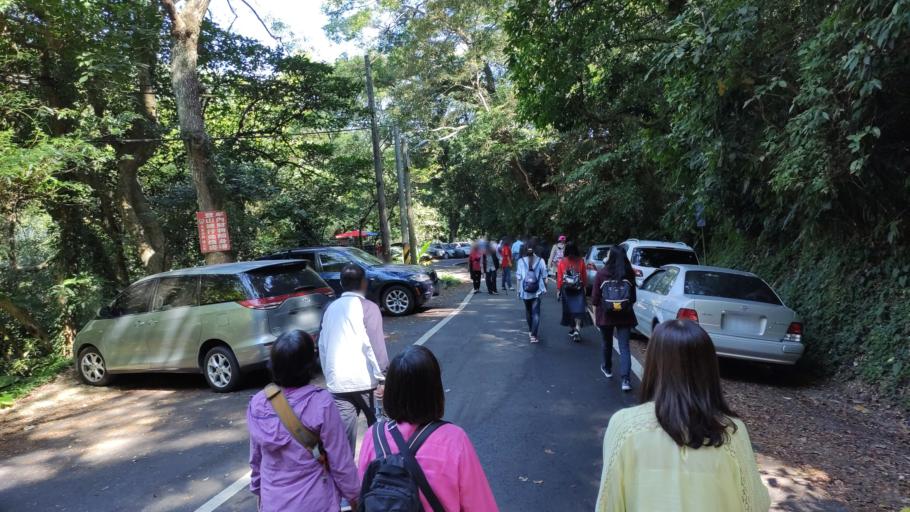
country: TW
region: Taiwan
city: Daxi
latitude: 24.8359
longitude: 121.3034
